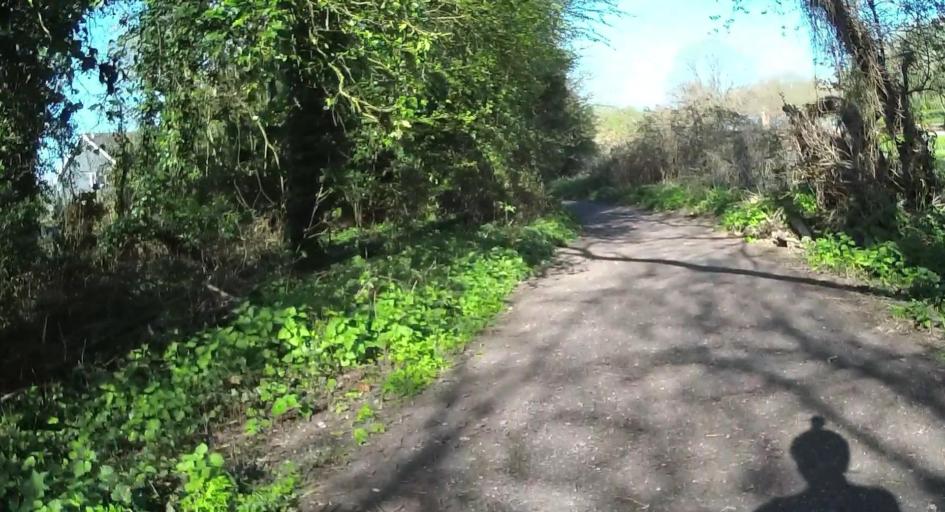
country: GB
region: England
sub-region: Hampshire
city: Abbotts Ann
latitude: 51.1115
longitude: -1.4901
